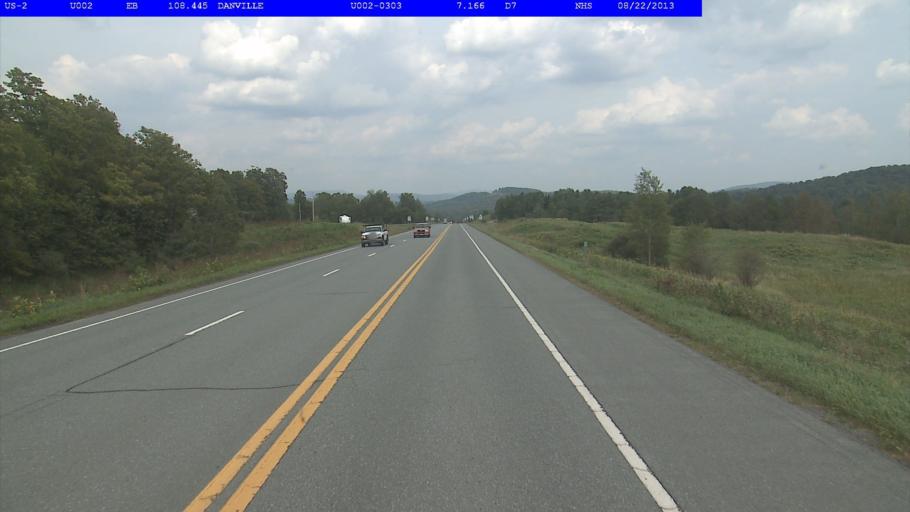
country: US
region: Vermont
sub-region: Caledonia County
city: St Johnsbury
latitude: 44.4321
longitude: -72.0944
